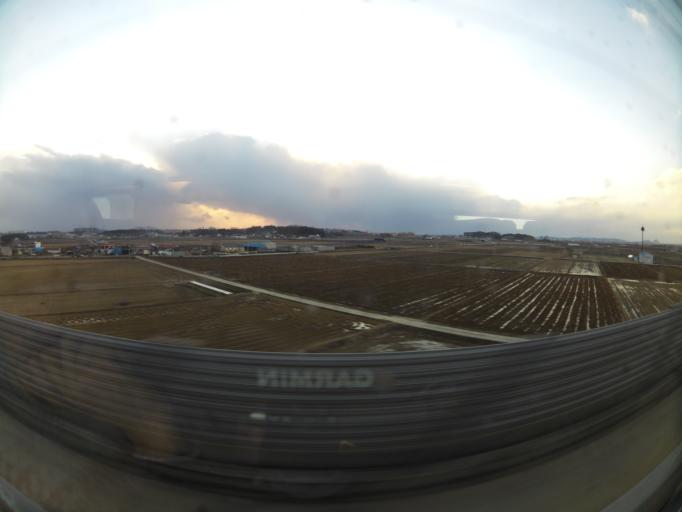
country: KR
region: Chungcheongnam-do
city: Seonghwan
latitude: 36.9857
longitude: 127.0590
